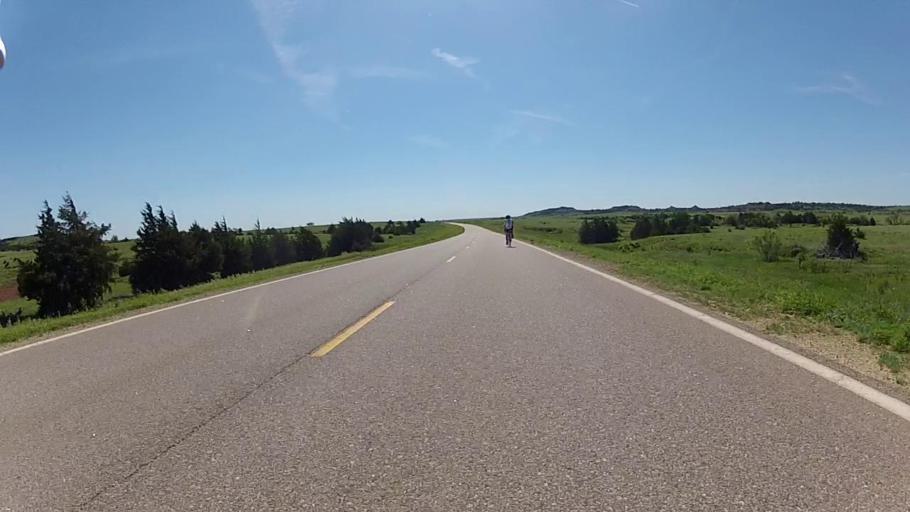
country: US
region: Kansas
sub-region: Barber County
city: Medicine Lodge
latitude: 37.2755
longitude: -98.7291
